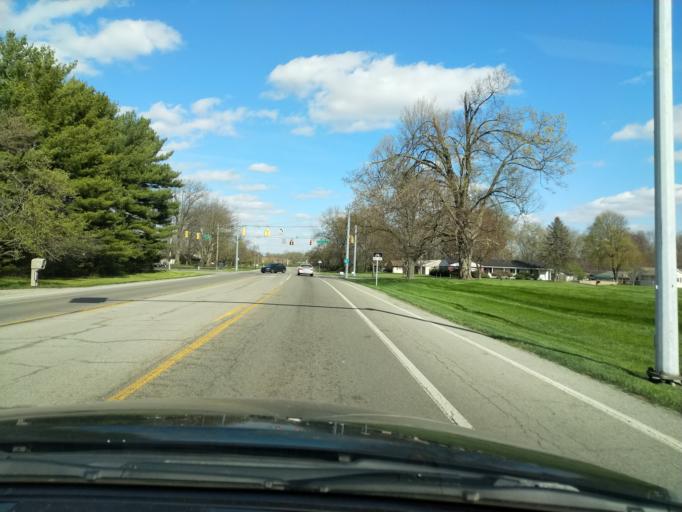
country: US
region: Indiana
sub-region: Marion County
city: Meridian Hills
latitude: 39.8852
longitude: -86.1896
